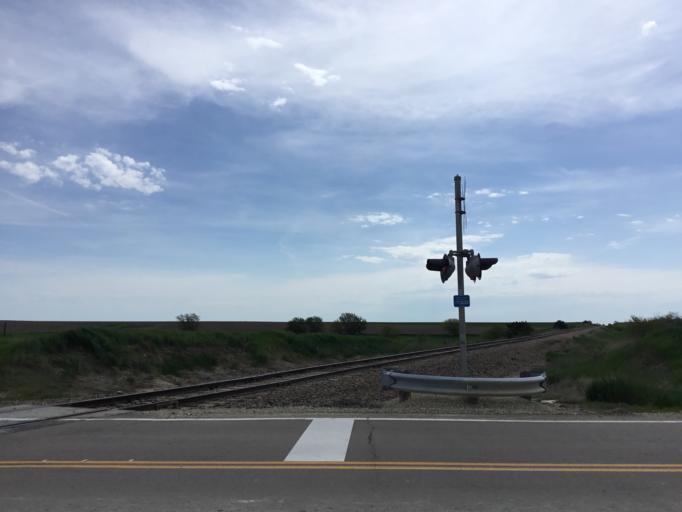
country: US
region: Kansas
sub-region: Mitchell County
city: Beloit
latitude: 39.5177
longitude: -98.3392
